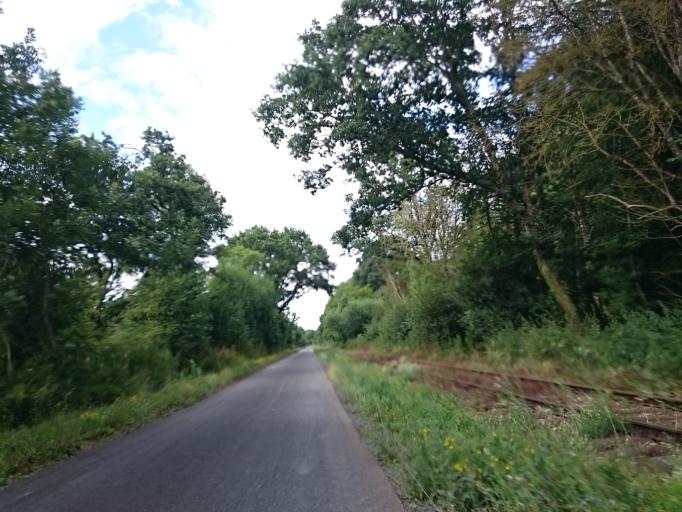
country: FR
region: Lower Normandy
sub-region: Departement du Calvados
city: Sainte-Honorine-du-Fay
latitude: 49.0393
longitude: -0.4642
